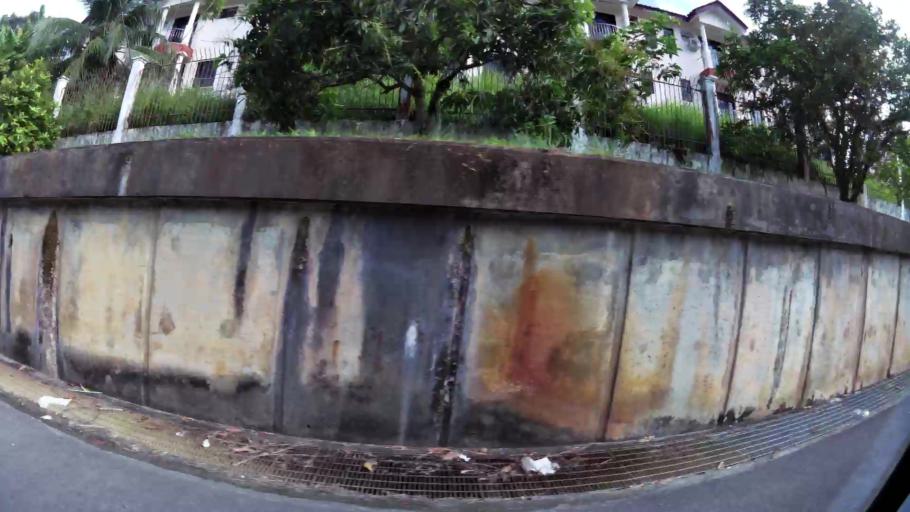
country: BN
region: Brunei and Muara
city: Bandar Seri Begawan
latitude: 4.8867
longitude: 114.9594
